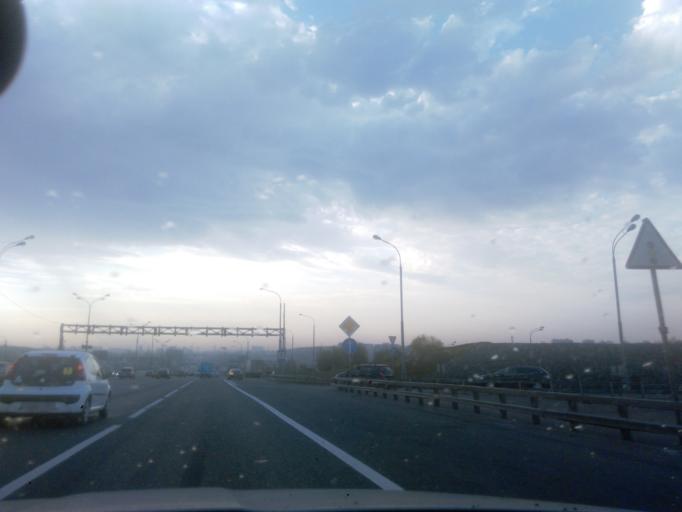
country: RU
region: Moskovskaya
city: Marfino
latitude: 55.7042
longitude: 37.3954
